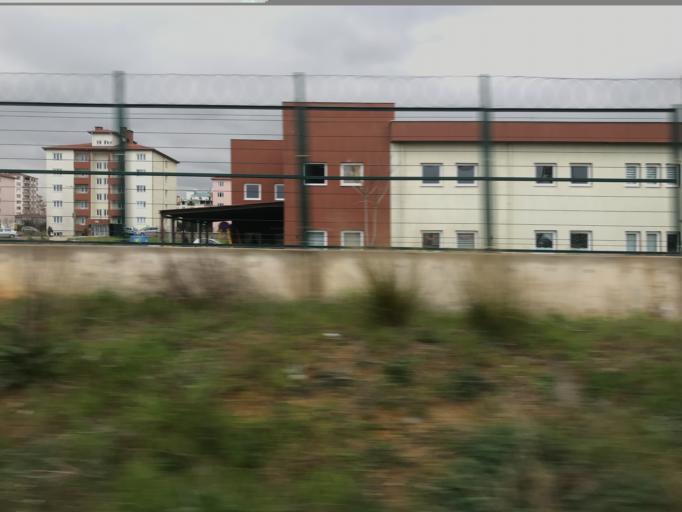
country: TR
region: Istanbul
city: Pendik
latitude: 40.8668
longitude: 29.2636
